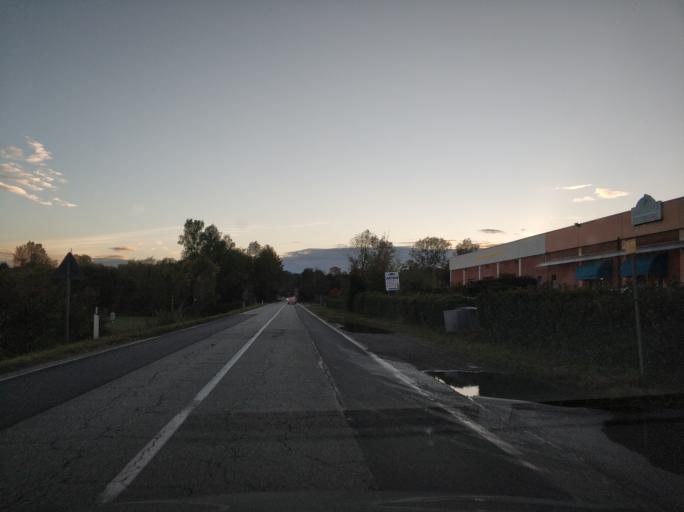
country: IT
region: Piedmont
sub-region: Provincia di Torino
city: Robassomero
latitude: 45.2069
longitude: 7.5759
